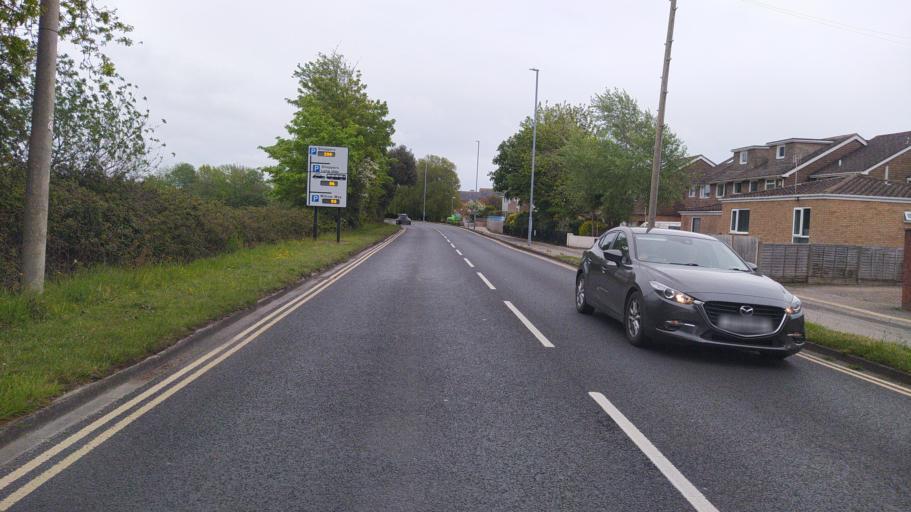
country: GB
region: England
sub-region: Dorset
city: Christchurch
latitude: 50.7312
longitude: -1.7852
